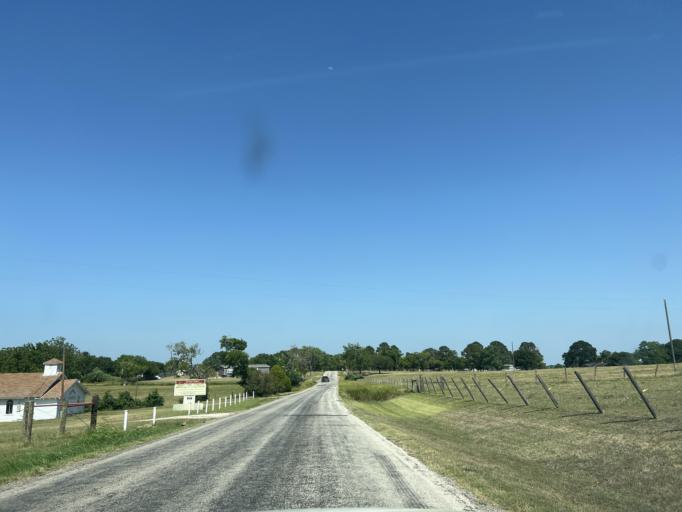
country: US
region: Texas
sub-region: Washington County
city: Brenham
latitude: 30.1721
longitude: -96.3669
